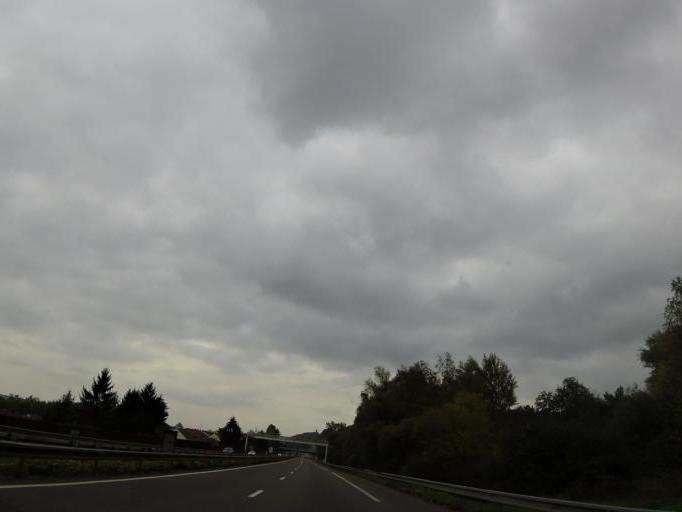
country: FR
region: Lorraine
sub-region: Departement de la Moselle
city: Morsbach
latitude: 49.1663
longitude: 6.8753
